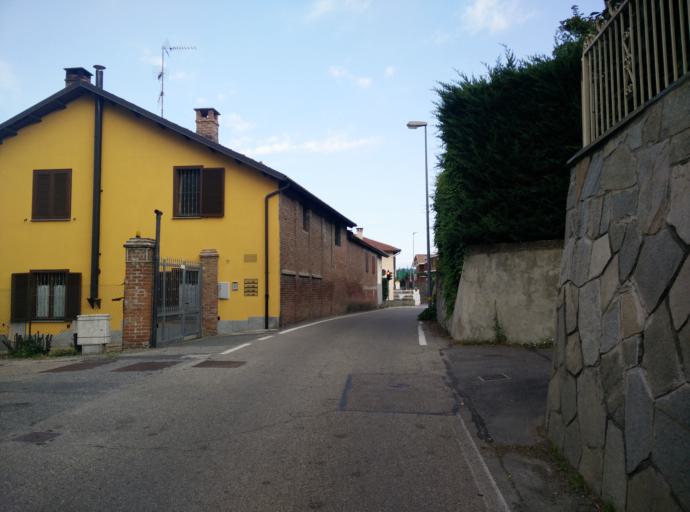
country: IT
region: Piedmont
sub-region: Provincia di Torino
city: Moncalieri
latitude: 44.9954
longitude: 7.7161
